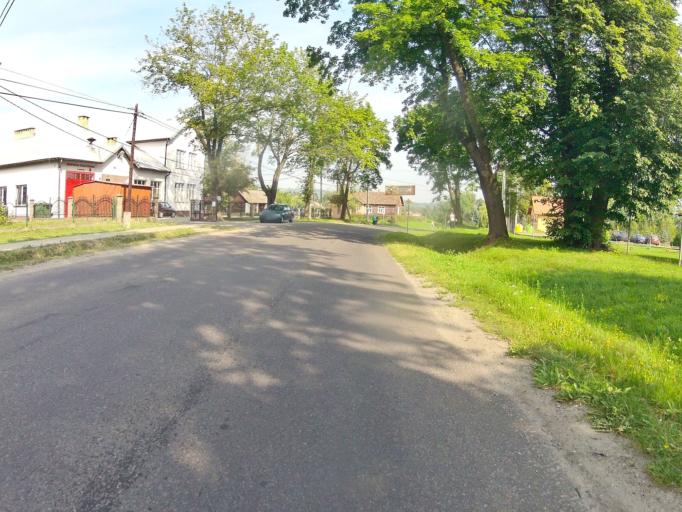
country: PL
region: Subcarpathian Voivodeship
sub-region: Powiat jasielski
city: Trzcinica
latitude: 49.7769
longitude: 21.4061
